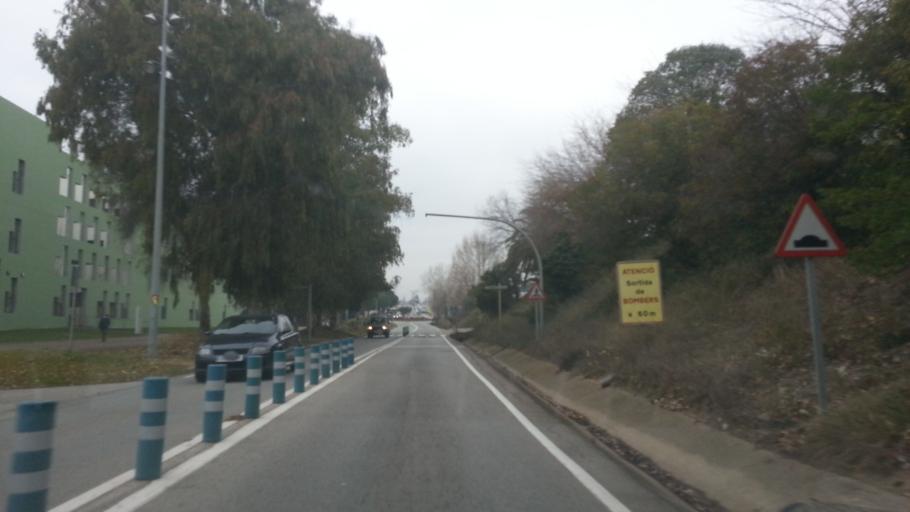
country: ES
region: Catalonia
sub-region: Provincia de Barcelona
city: Barbera del Valles
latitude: 41.5012
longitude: 2.1123
